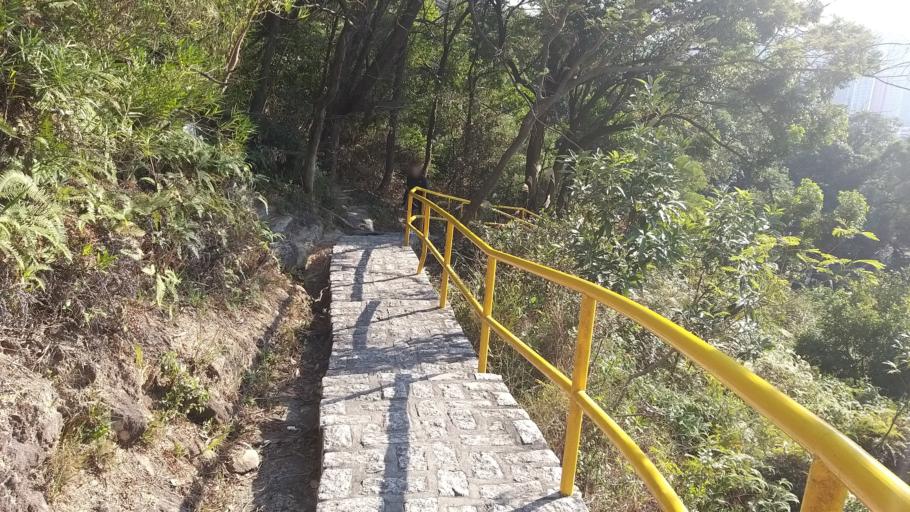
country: HK
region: Tuen Mun
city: Tuen Mun
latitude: 22.3955
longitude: 113.9831
